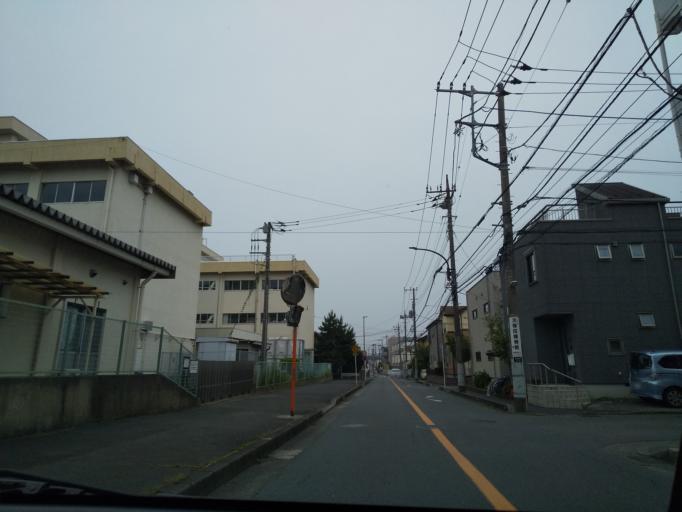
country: JP
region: Kanagawa
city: Zama
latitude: 35.5064
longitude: 139.4038
